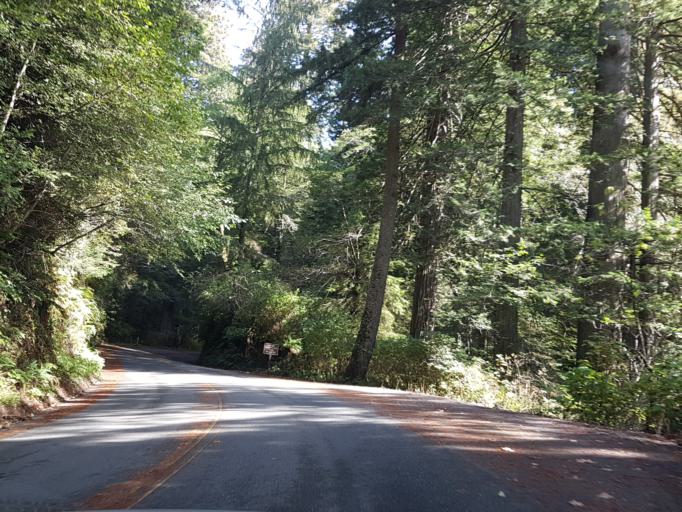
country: US
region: California
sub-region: Del Norte County
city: Bertsch-Oceanview
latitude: 41.4517
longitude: -124.0407
